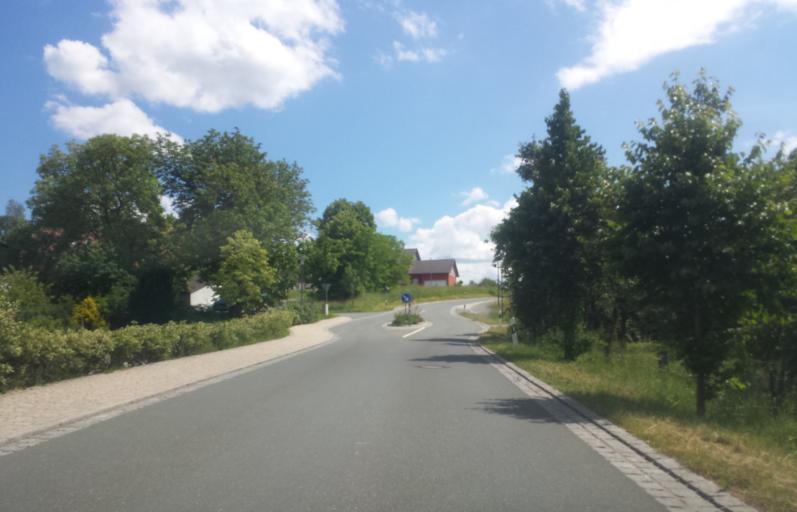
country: DE
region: Bavaria
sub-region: Upper Franconia
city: Hallerndorf
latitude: 49.7849
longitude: 10.9567
